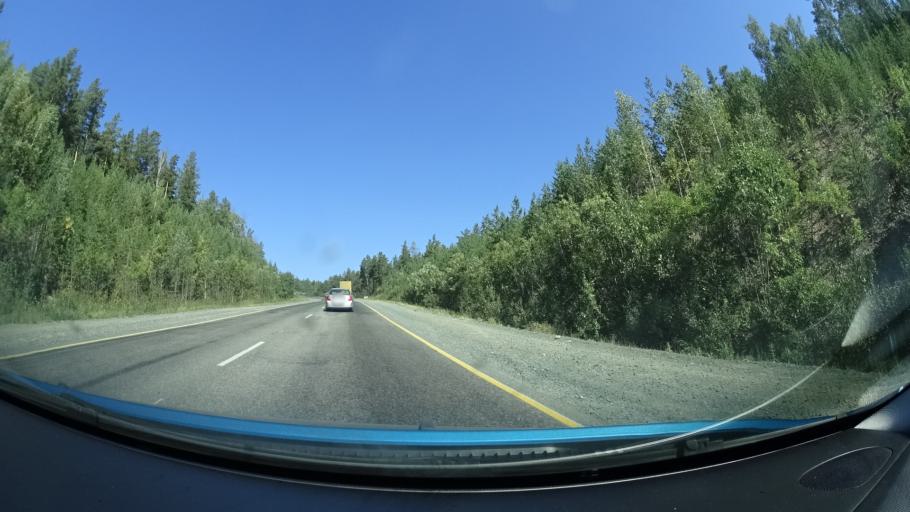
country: RU
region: Bashkortostan
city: Abzakovo
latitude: 53.8849
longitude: 58.5286
